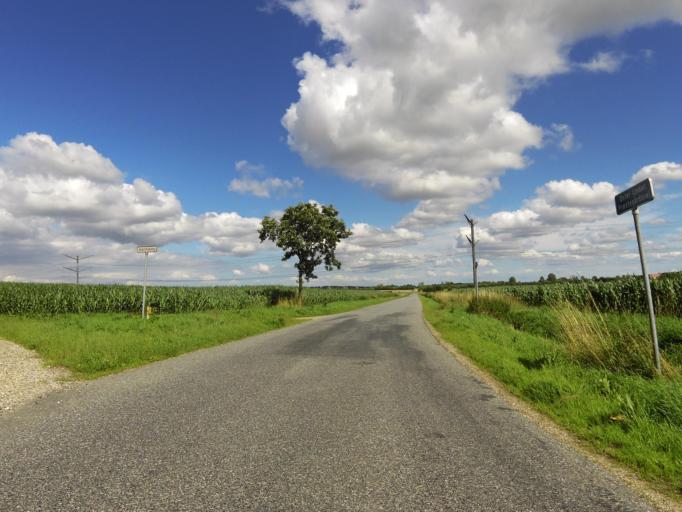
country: DK
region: South Denmark
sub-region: Vejen Kommune
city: Rodding
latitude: 55.3148
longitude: 9.1594
